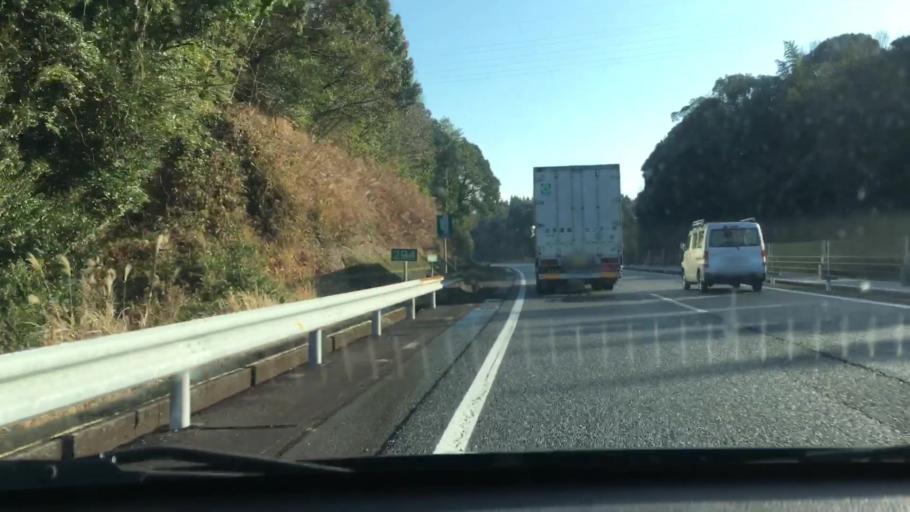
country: JP
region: Kagoshima
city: Okuchi-shinohara
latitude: 31.9153
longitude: 130.7033
